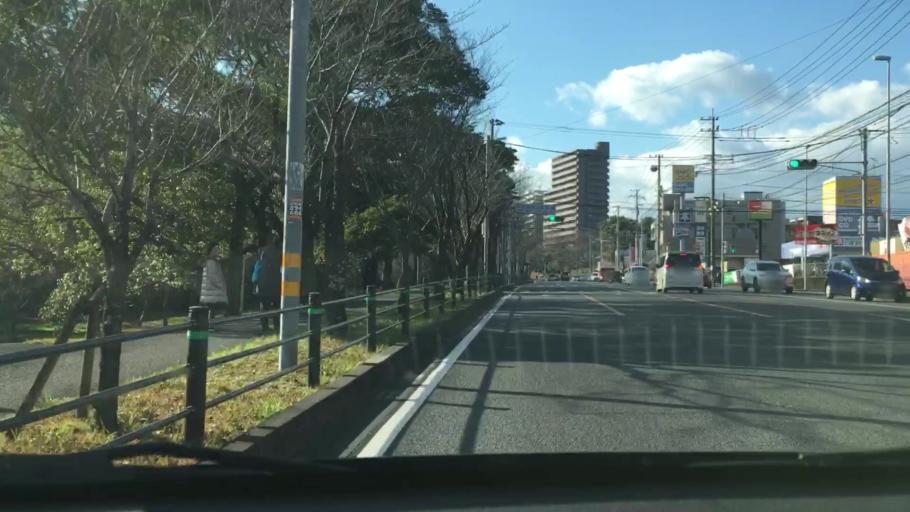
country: JP
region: Oita
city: Tsurusaki
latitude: 33.2253
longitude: 131.6586
